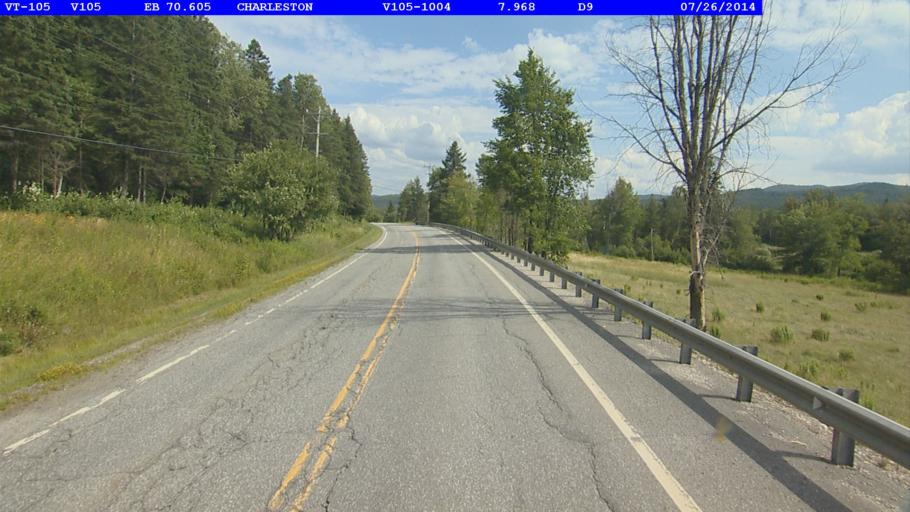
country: US
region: Vermont
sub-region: Orleans County
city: Newport
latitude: 44.8299
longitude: -71.9777
